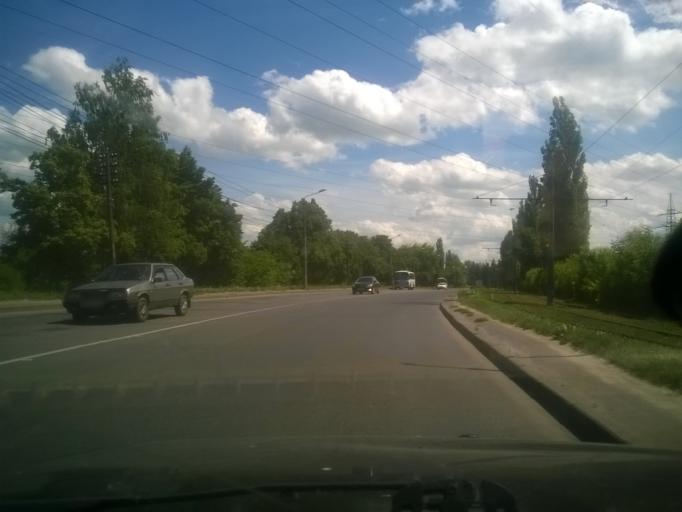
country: RU
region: Kursk
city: Kursk
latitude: 51.6660
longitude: 36.1173
